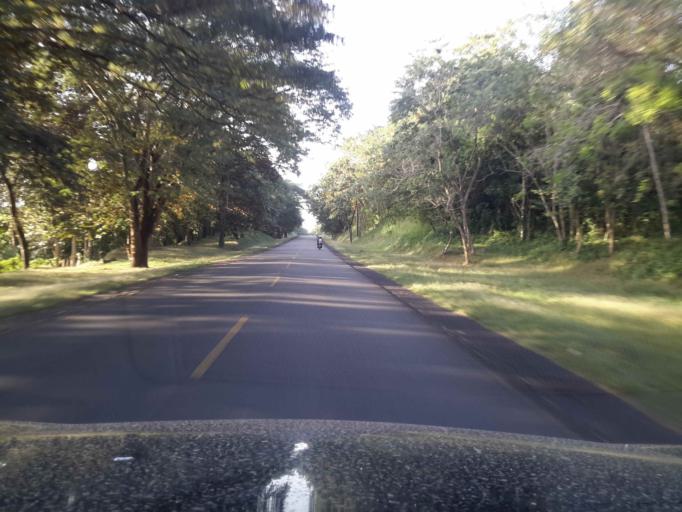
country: NI
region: Rio San Juan
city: San Miguelito
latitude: 11.4062
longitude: -84.8330
